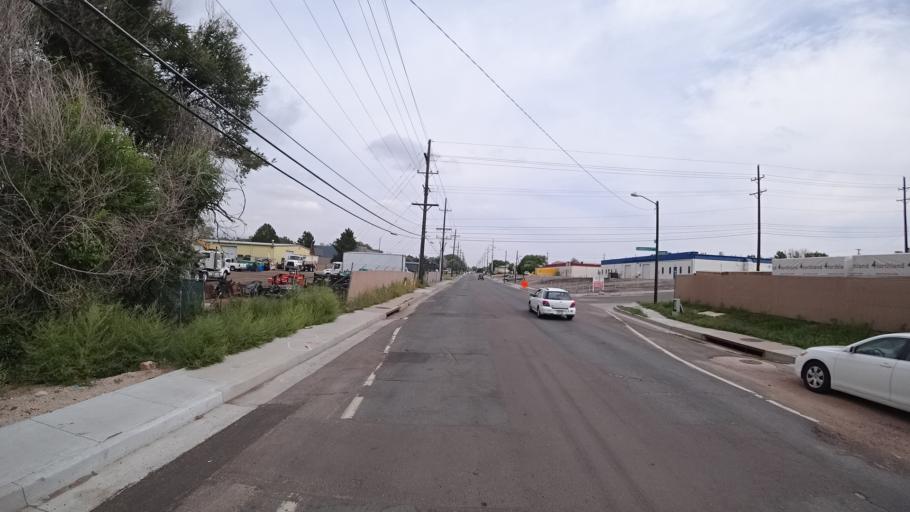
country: US
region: Colorado
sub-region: El Paso County
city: Colorado Springs
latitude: 38.8790
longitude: -104.8228
